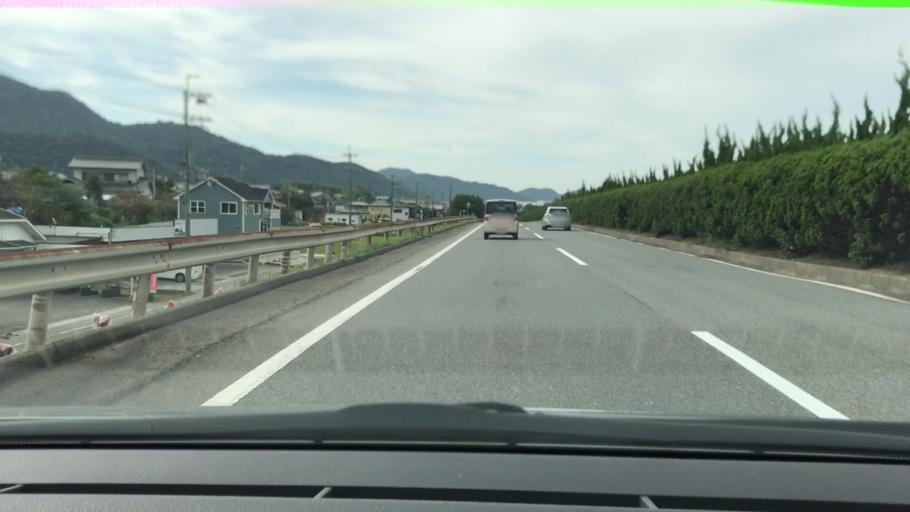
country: JP
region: Hyogo
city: Himeji
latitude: 34.9084
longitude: 134.7537
